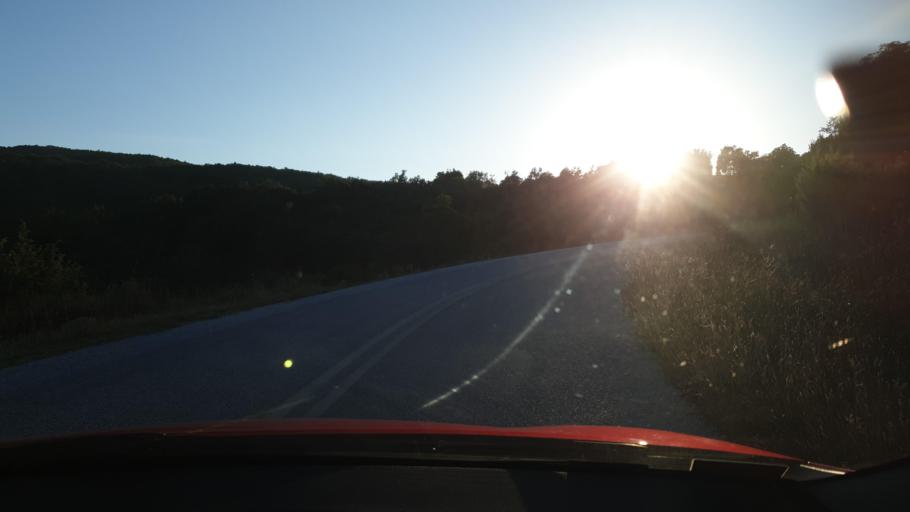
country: GR
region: Central Macedonia
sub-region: Nomos Chalkidikis
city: Galatista
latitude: 40.5182
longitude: 23.2750
